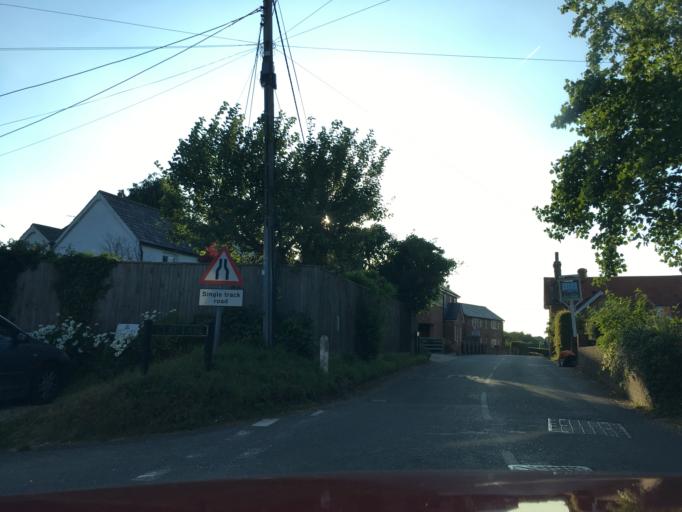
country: GB
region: England
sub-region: Hampshire
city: Tadley
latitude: 51.4160
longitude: -1.1609
